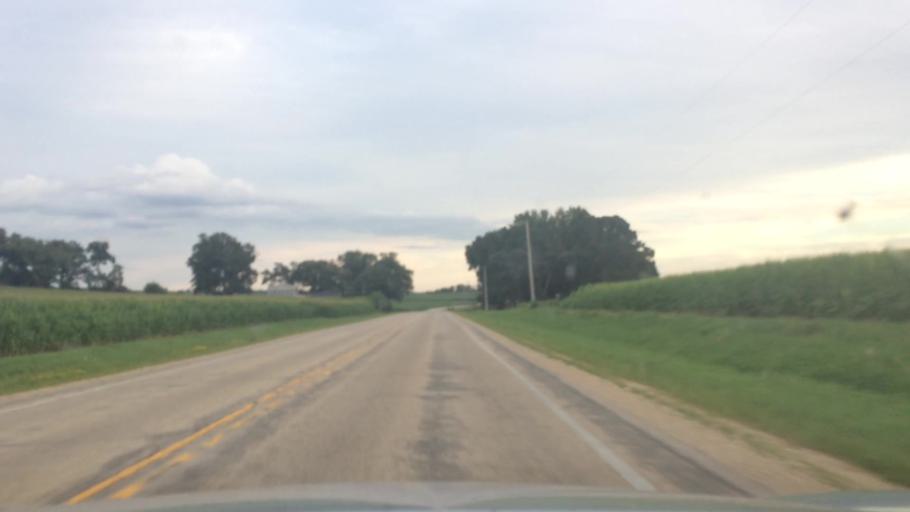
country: US
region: Wisconsin
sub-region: Dane County
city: Waunakee
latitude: 43.2185
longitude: -89.5462
